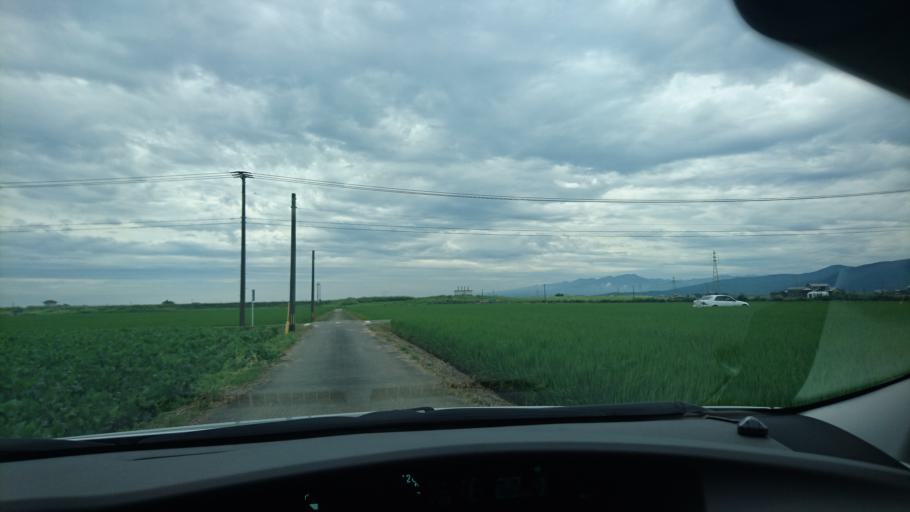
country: JP
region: Saga Prefecture
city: Takeocho-takeo
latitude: 33.2101
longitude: 130.1269
